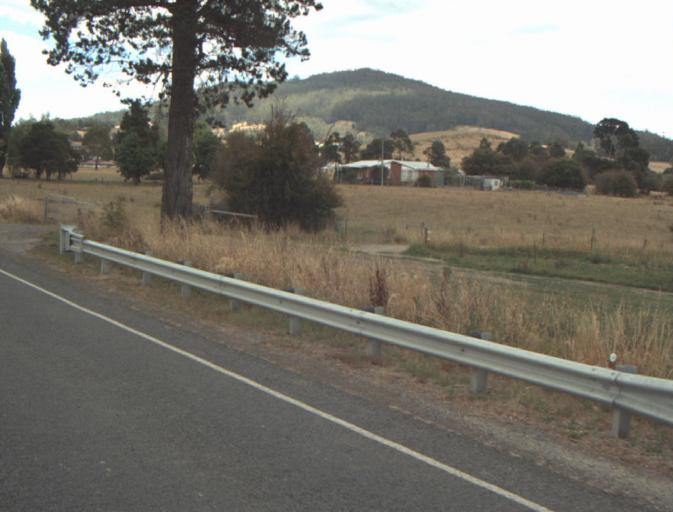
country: AU
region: Tasmania
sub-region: Launceston
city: Mayfield
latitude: -41.2453
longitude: 147.2172
